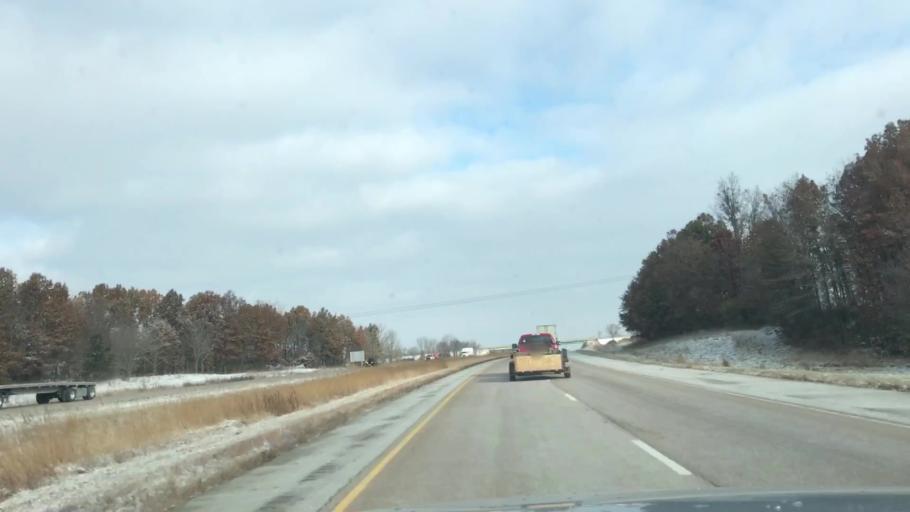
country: US
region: Illinois
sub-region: Macoupin County
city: Staunton
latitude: 39.0378
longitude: -89.7553
